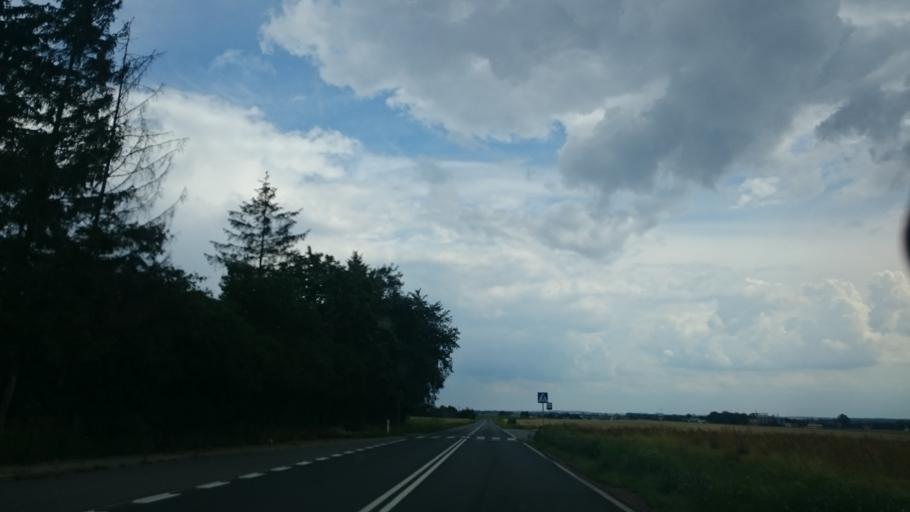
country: PL
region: Kujawsko-Pomorskie
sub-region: Powiat tucholski
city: Kesowo
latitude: 53.6624
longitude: 17.6746
